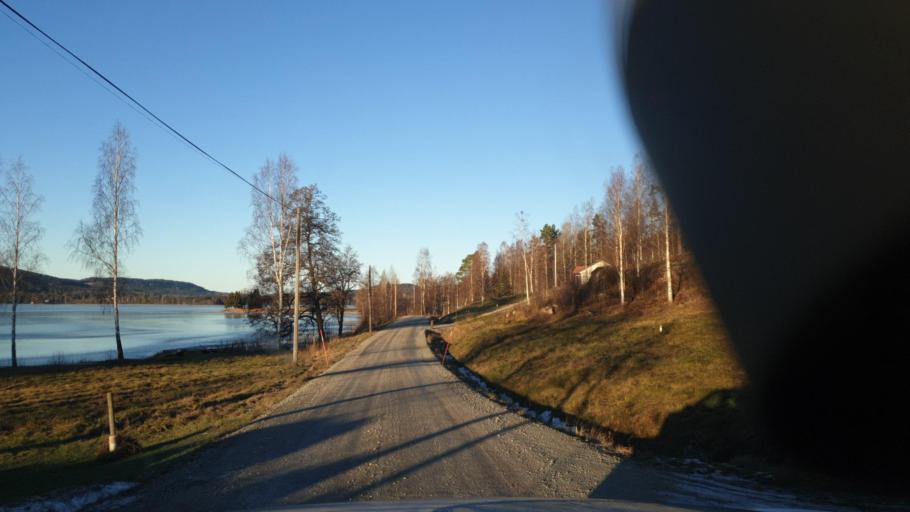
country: SE
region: Vaermland
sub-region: Arvika Kommun
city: Arvika
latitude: 59.7232
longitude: 12.8373
